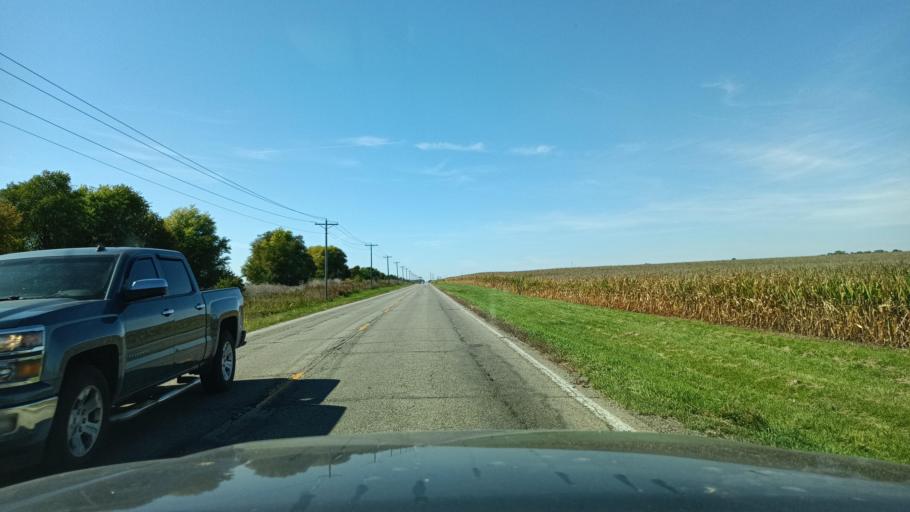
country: US
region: Illinois
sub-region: Champaign County
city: Mahomet
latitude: 40.2005
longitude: -88.4488
